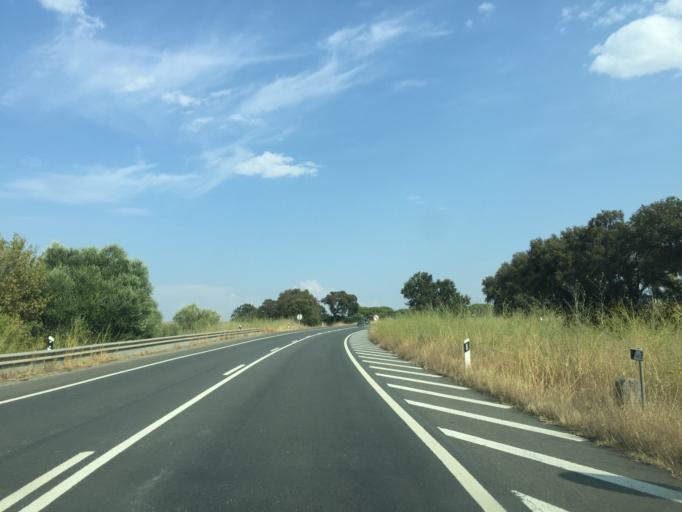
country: PT
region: Setubal
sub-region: Grandola
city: Grandola
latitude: 38.0109
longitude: -8.3816
